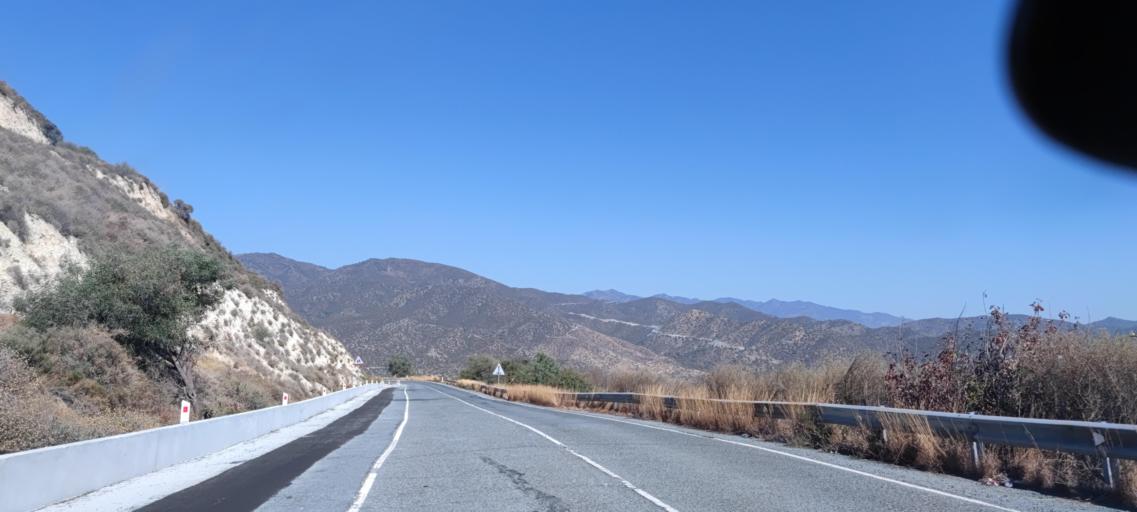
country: CY
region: Limassol
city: Mouttagiaka
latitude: 34.7580
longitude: 33.0635
